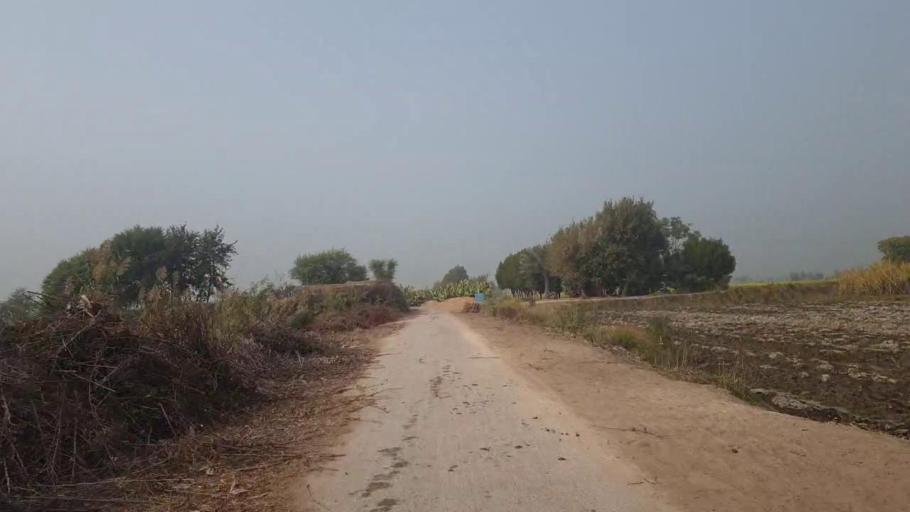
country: PK
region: Sindh
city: Bhit Shah
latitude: 25.8218
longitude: 68.5624
